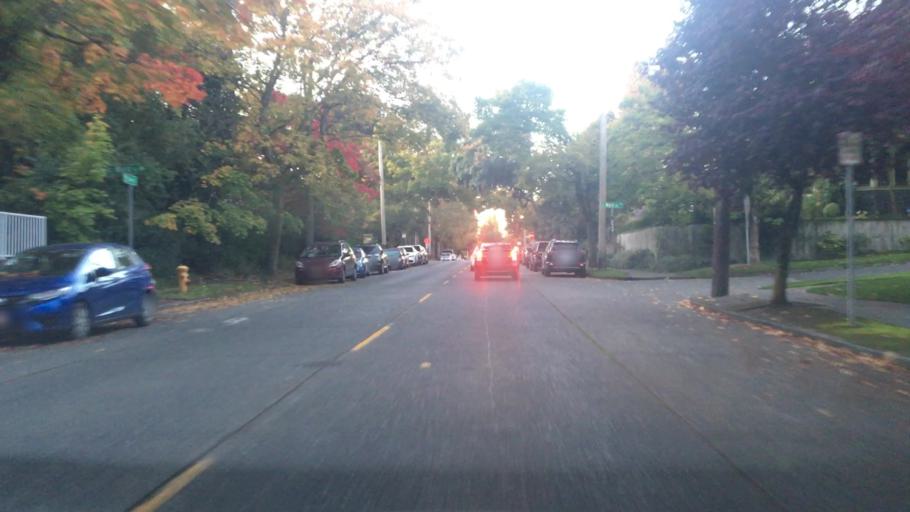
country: US
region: Washington
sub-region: King County
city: Seattle
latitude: 47.6279
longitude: -122.3126
